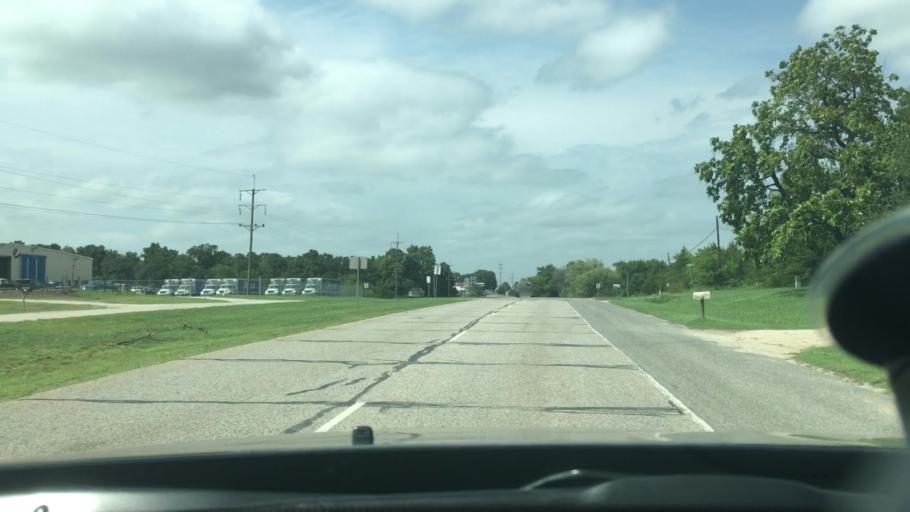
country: US
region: Oklahoma
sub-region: Pontotoc County
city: Ada
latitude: 34.8137
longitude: -96.6784
